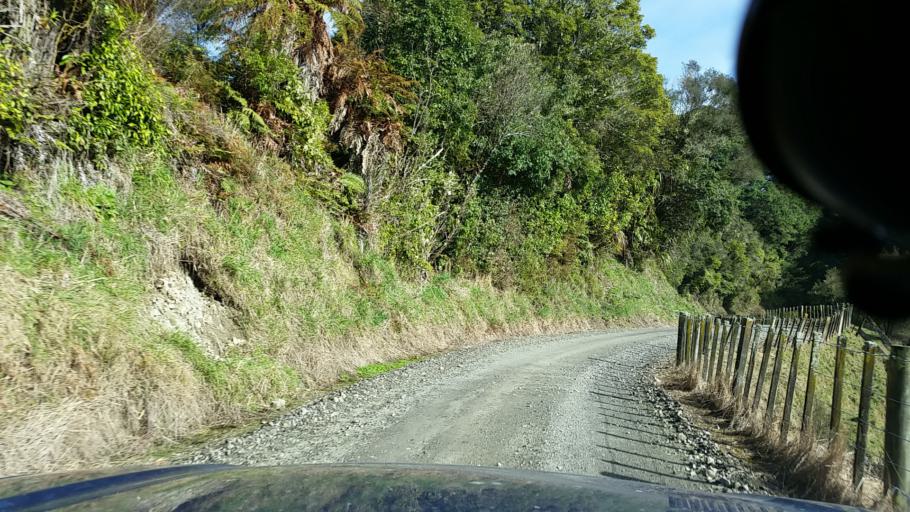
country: NZ
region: Taranaki
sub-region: New Plymouth District
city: Waitara
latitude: -39.0348
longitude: 174.7825
